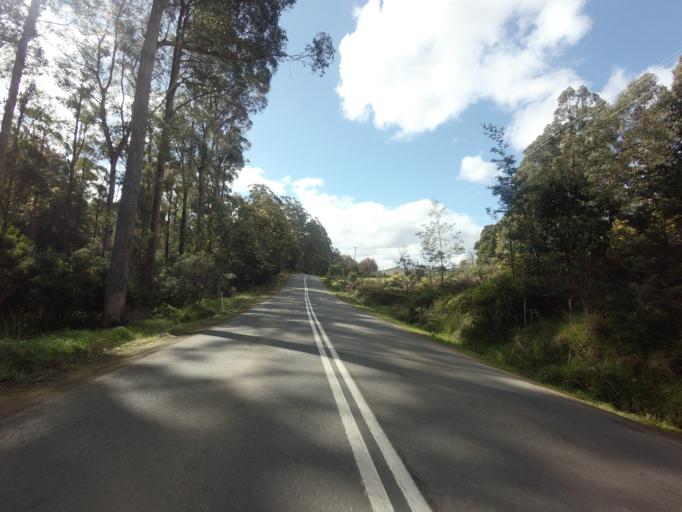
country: AU
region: Tasmania
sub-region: Huon Valley
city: Geeveston
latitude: -43.2213
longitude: 146.9878
